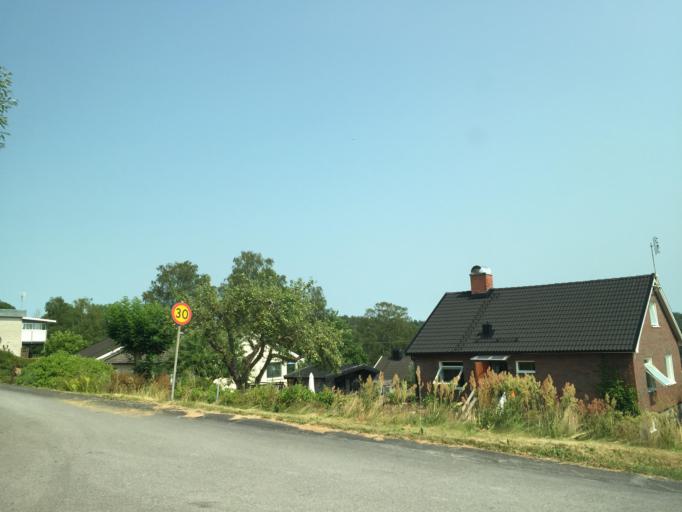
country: SE
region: Vaestra Goetaland
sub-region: Lilla Edets Kommun
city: Lilla Edet
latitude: 58.1809
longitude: 12.1136
